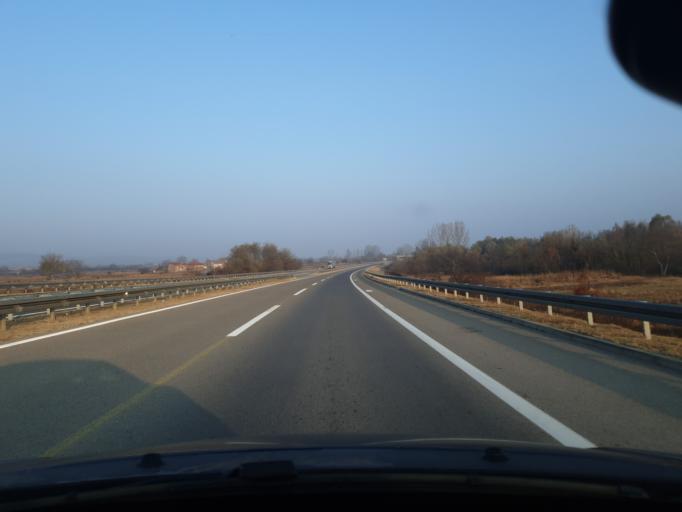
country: RS
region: Central Serbia
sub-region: Jablanicki Okrug
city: Vlasotince
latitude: 42.9175
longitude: 22.0337
